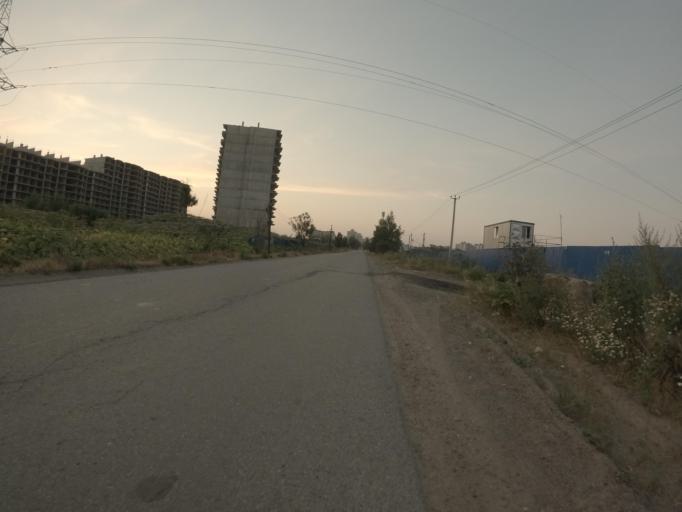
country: RU
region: Leningrad
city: Yanino Vtoroye
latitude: 59.9420
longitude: 30.5532
